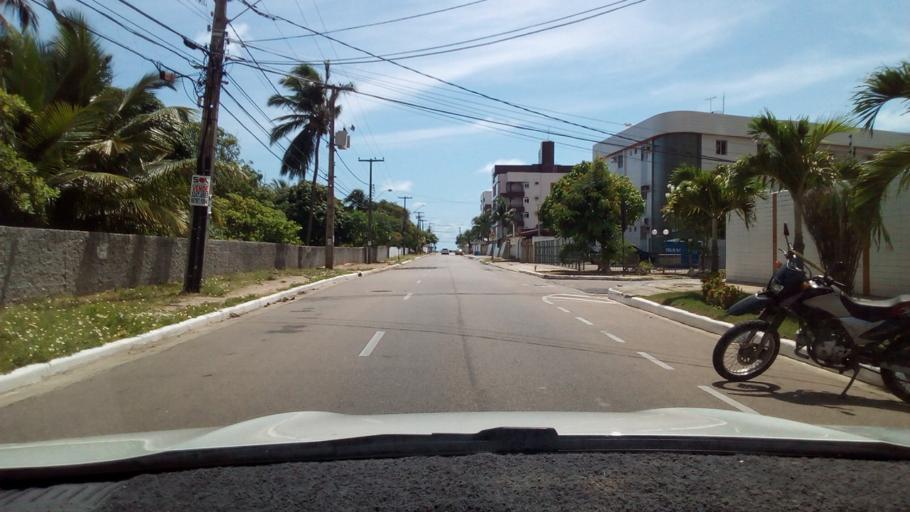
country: BR
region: Paraiba
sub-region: Joao Pessoa
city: Joao Pessoa
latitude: -7.0742
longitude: -34.8343
